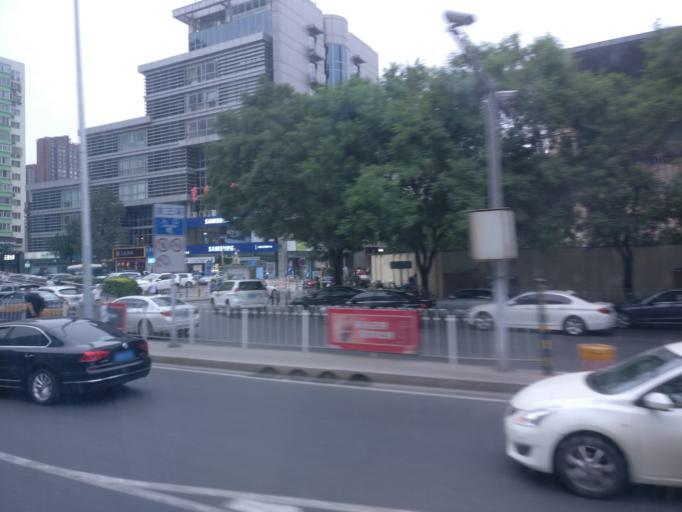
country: CN
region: Beijing
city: Longtan
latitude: 39.8946
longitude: 116.4555
